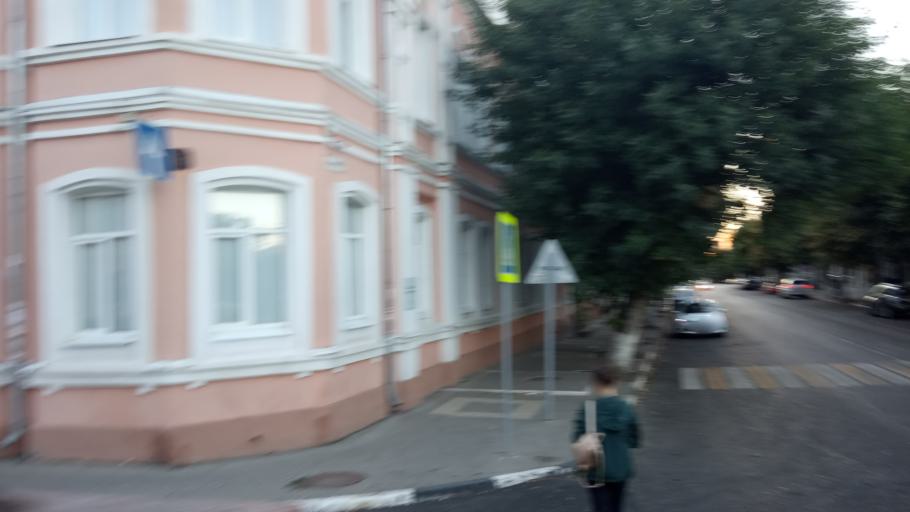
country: RU
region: Voronezj
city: Voronezh
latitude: 51.6612
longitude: 39.2075
